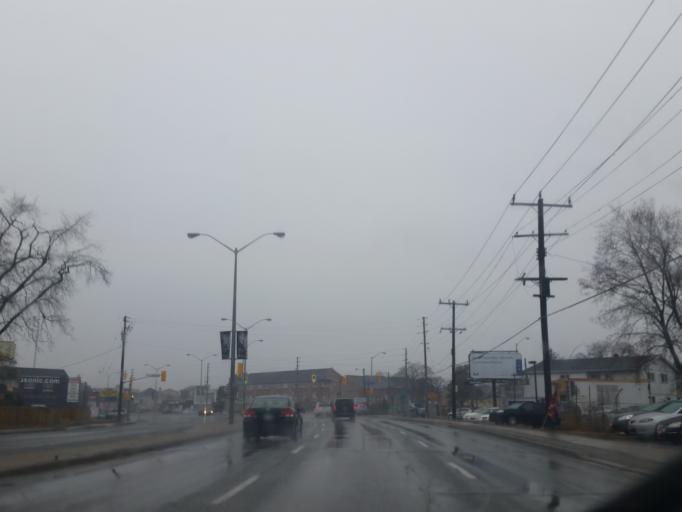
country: CA
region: Ontario
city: Scarborough
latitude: 43.7744
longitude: -79.1819
